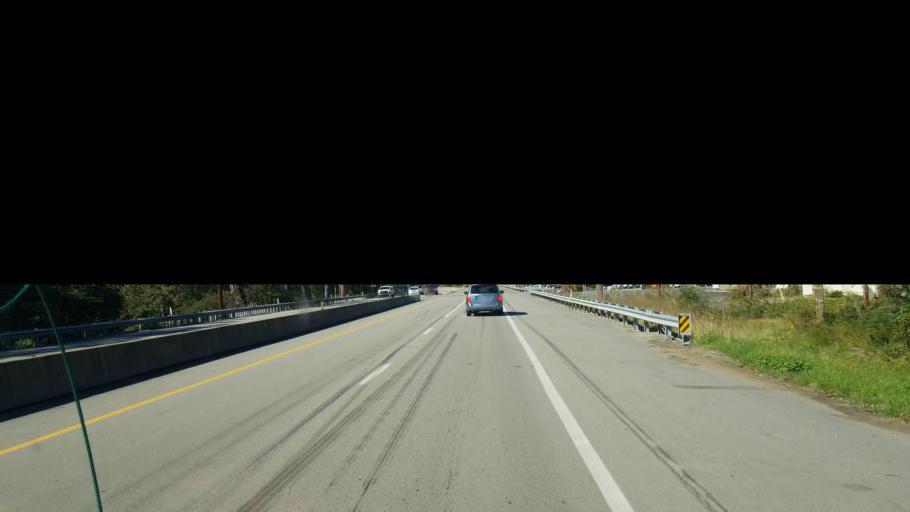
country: US
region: Pennsylvania
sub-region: Westmoreland County
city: Ligonier
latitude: 40.2449
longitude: -79.2439
